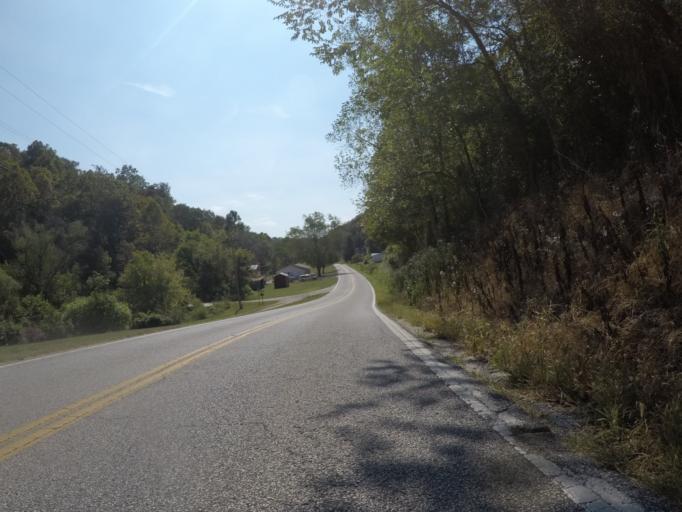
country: US
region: West Virginia
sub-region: Cabell County
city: Lesage
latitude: 38.5646
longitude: -82.3966
